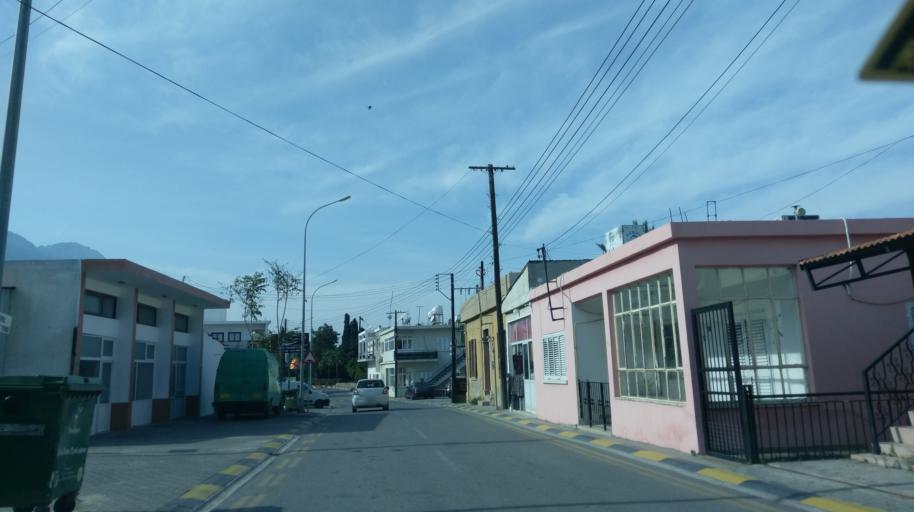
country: CY
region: Keryneia
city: Lapithos
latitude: 35.3403
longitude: 33.1808
